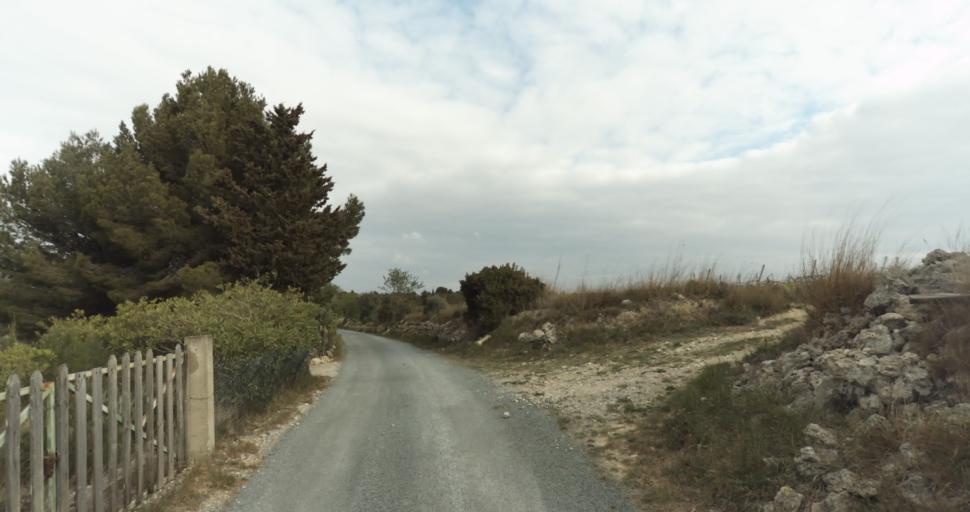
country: FR
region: Languedoc-Roussillon
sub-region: Departement de l'Aude
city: Leucate
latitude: 42.9299
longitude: 3.0253
